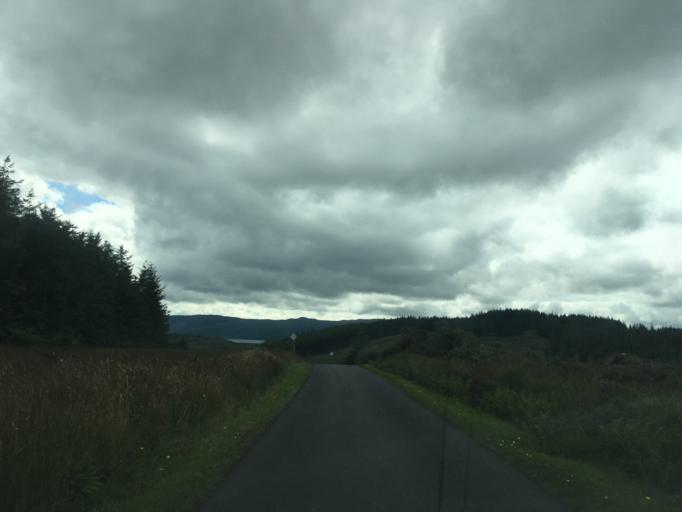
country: GB
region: Scotland
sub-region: Argyll and Bute
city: Tarbert
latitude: 55.8786
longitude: -5.2772
